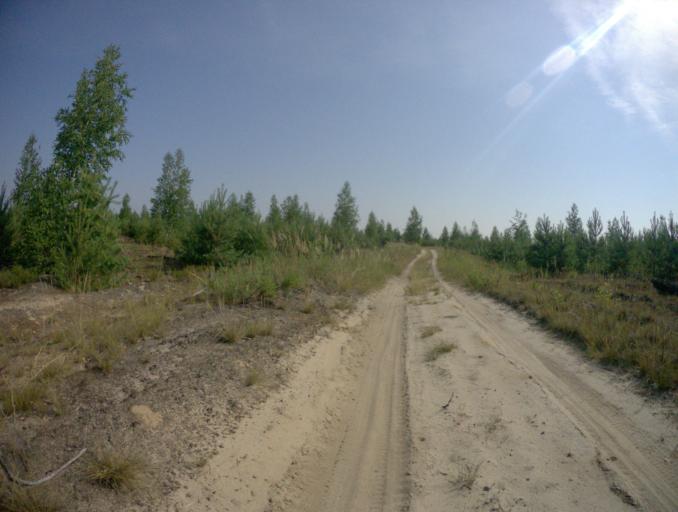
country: RU
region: Ivanovo
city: Talitsy
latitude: 56.4107
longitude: 42.3015
